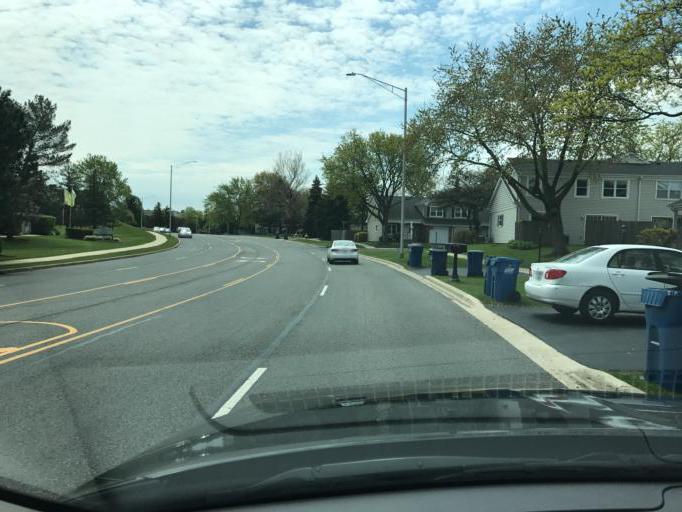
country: US
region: Illinois
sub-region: DuPage County
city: Naperville
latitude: 41.7776
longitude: -88.1097
